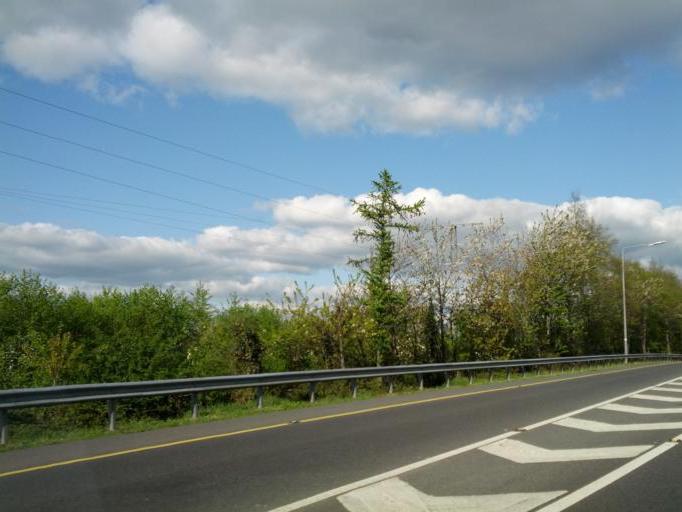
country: IE
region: Leinster
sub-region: An Iarmhi
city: Athlone
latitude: 53.4348
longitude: -7.9439
